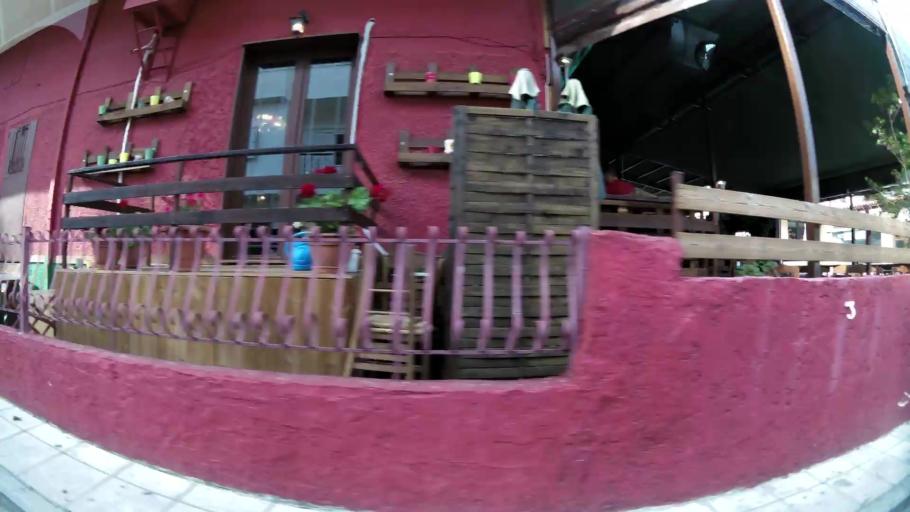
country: GR
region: Central Macedonia
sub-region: Nomos Thessalonikis
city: Oraiokastro
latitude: 40.7303
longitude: 22.9167
